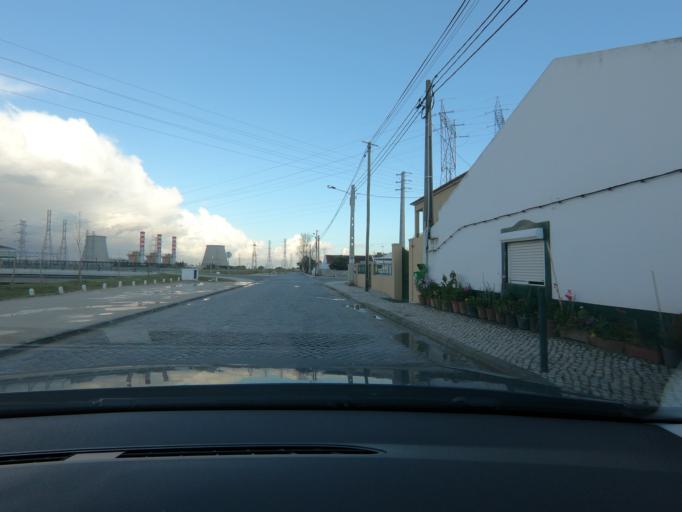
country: PT
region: Lisbon
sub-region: Alenquer
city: Carregado
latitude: 39.0114
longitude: -8.9619
